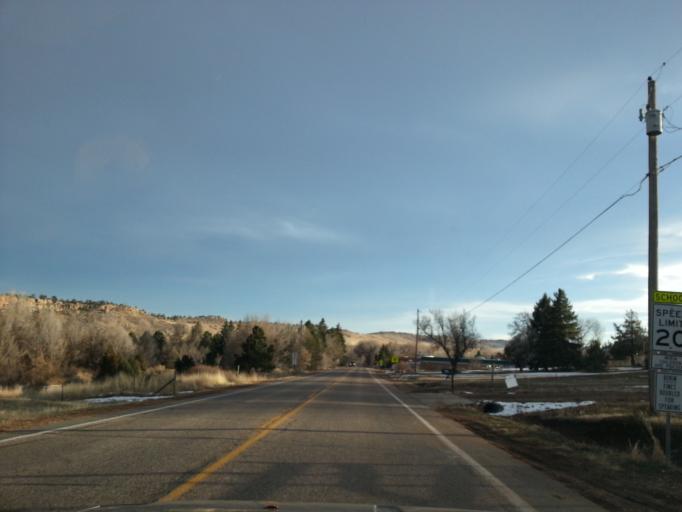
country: US
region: Colorado
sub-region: Larimer County
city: Loveland
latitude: 40.4206
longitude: -105.1897
